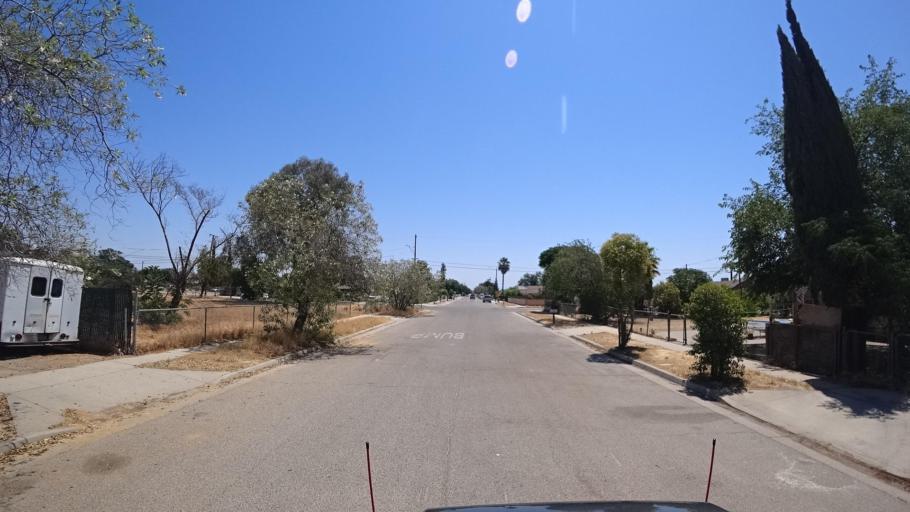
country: US
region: California
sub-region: Fresno County
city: West Park
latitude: 36.7087
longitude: -119.8140
